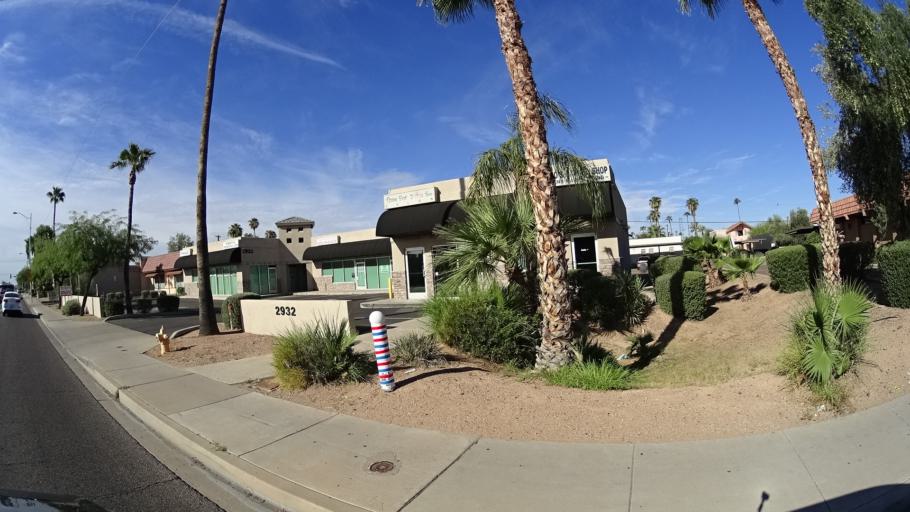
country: US
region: Arizona
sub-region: Maricopa County
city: Scottsdale
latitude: 33.4818
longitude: -111.9348
